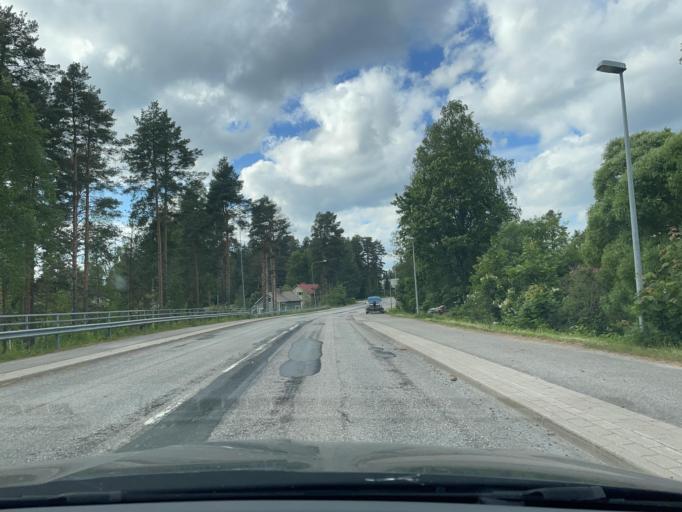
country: FI
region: Central Finland
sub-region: Jaemsae
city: Jaemsaenkoski
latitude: 61.9333
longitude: 25.1619
